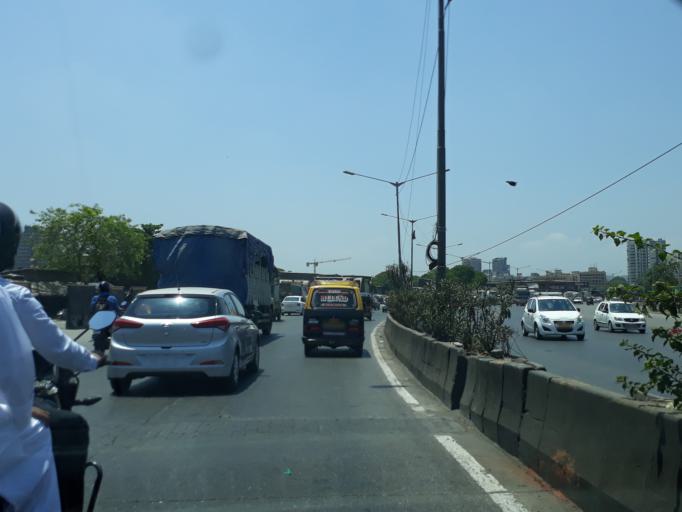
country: IN
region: Maharashtra
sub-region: Mumbai Suburban
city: Mumbai
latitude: 19.0702
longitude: 72.9083
